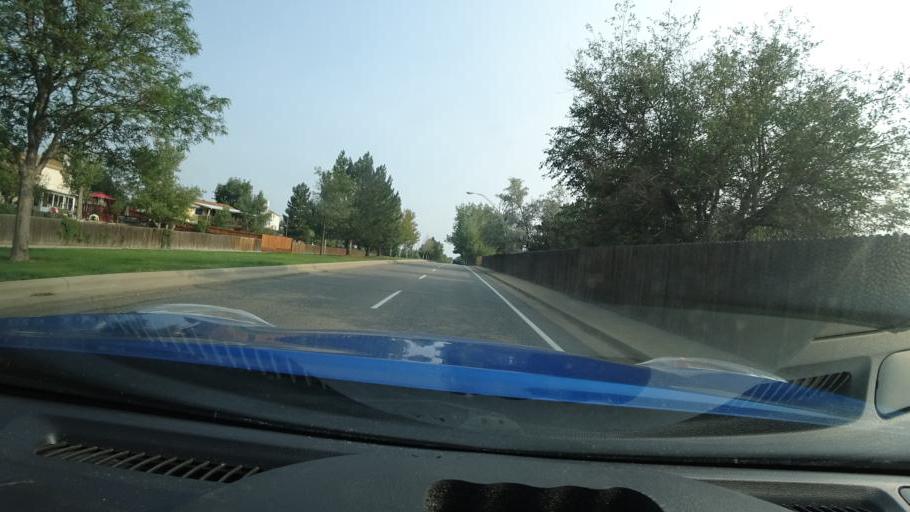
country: US
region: Colorado
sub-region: Adams County
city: Aurora
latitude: 39.6665
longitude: -104.7912
